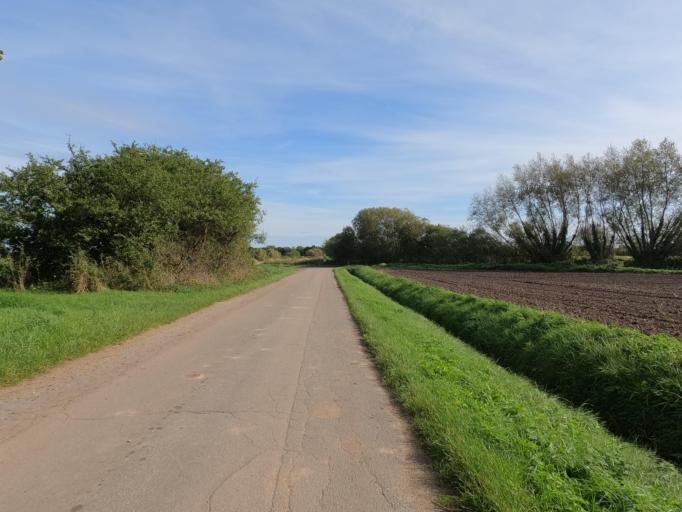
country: DE
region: Schleswig-Holstein
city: Riepsdorf
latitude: 54.2324
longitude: 10.9800
